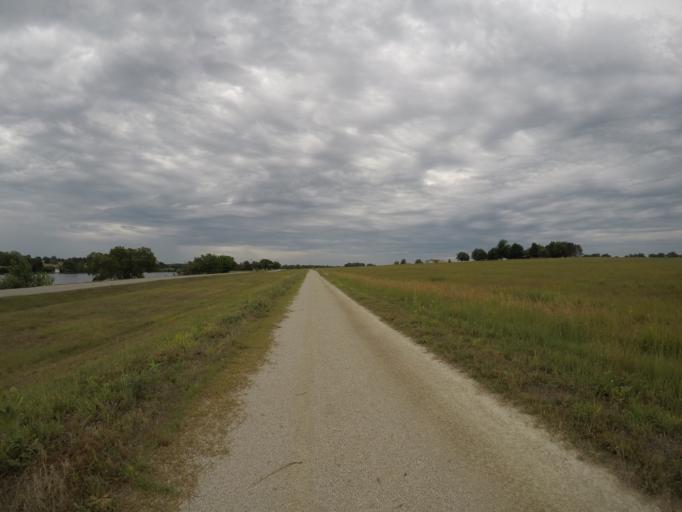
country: US
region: Kansas
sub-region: Anderson County
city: Garnett
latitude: 38.3024
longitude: -95.2448
